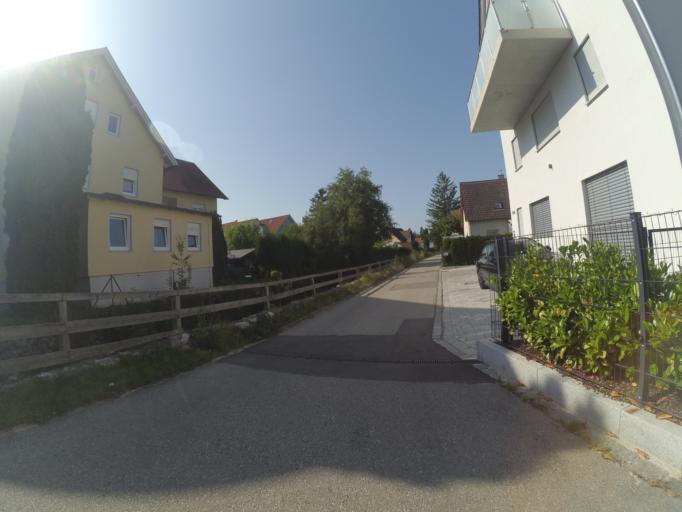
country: DE
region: Bavaria
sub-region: Swabia
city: Buchloe
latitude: 48.0381
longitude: 10.7252
